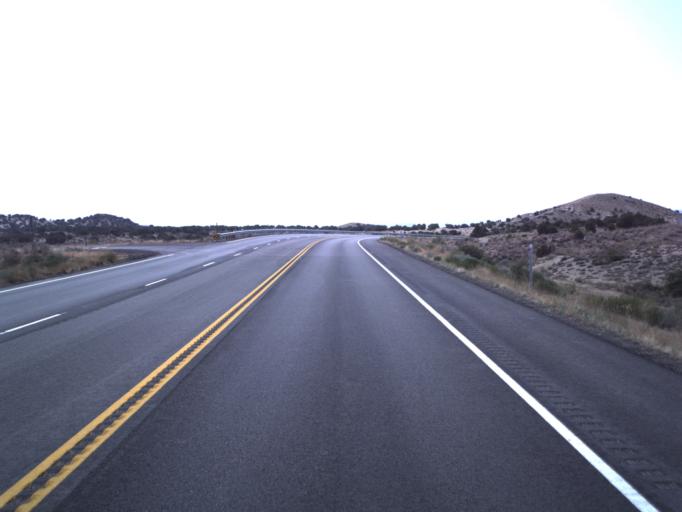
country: US
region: Utah
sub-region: Uintah County
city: Naples
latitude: 40.3447
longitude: -109.4856
